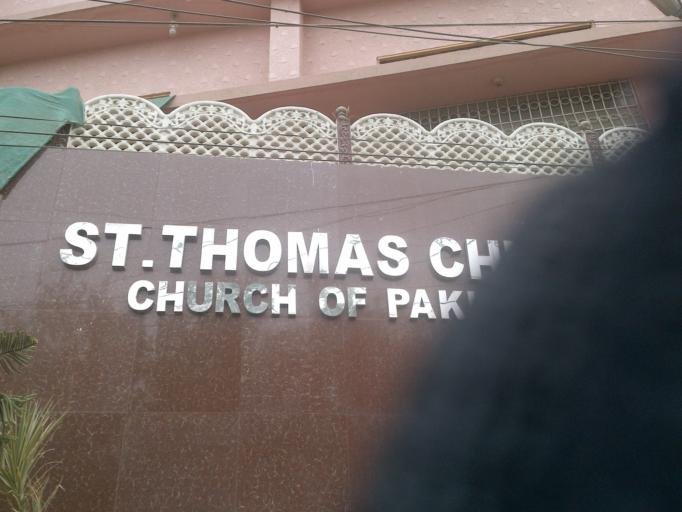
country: PK
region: Sindh
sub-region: Karachi District
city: Karachi
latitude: 24.8480
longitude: 67.0669
